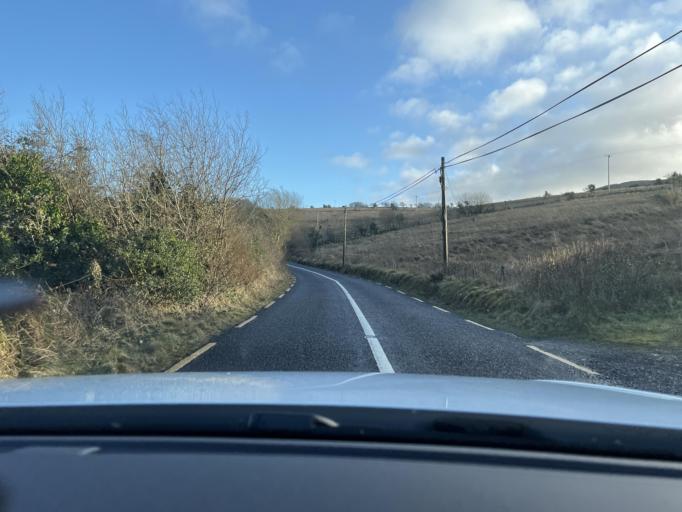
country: IE
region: Connaught
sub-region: County Leitrim
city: Manorhamilton
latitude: 54.2009
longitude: -7.9571
